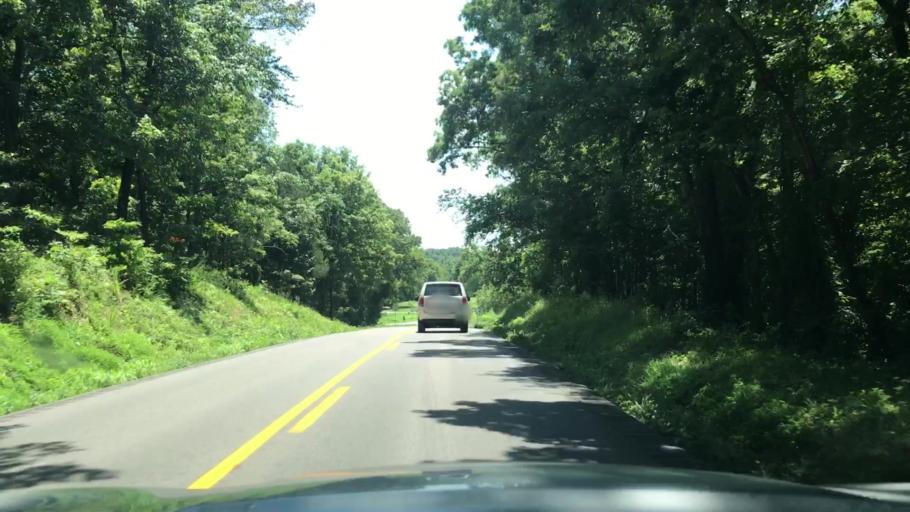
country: US
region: Kentucky
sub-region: Christian County
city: Hopkinsville
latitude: 36.8948
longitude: -87.4520
